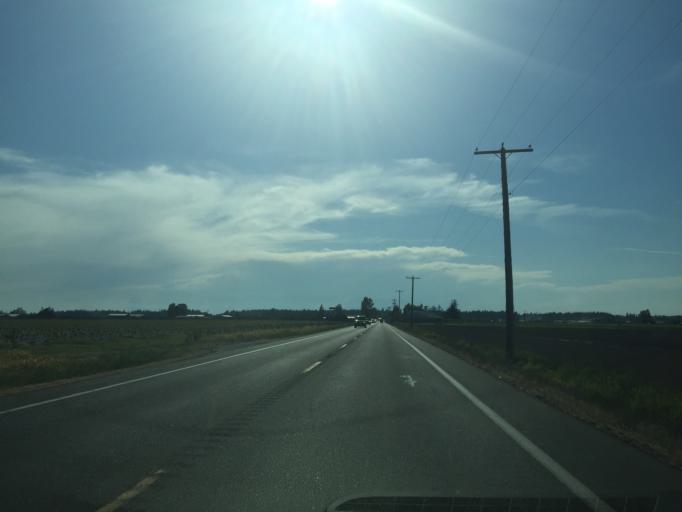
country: US
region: Washington
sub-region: Whatcom County
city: Lynden
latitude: 48.9645
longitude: -122.4754
